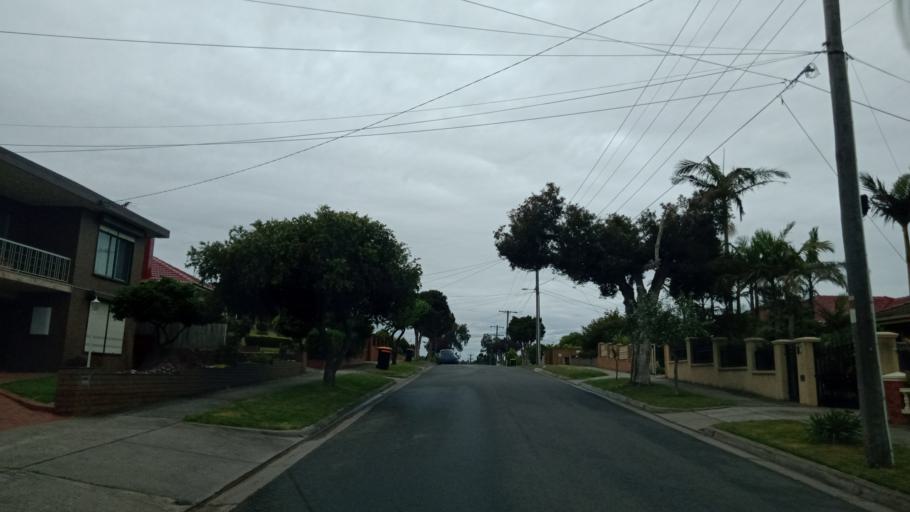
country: AU
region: Victoria
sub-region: Greater Dandenong
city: Springvale
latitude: -37.9427
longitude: 145.1590
